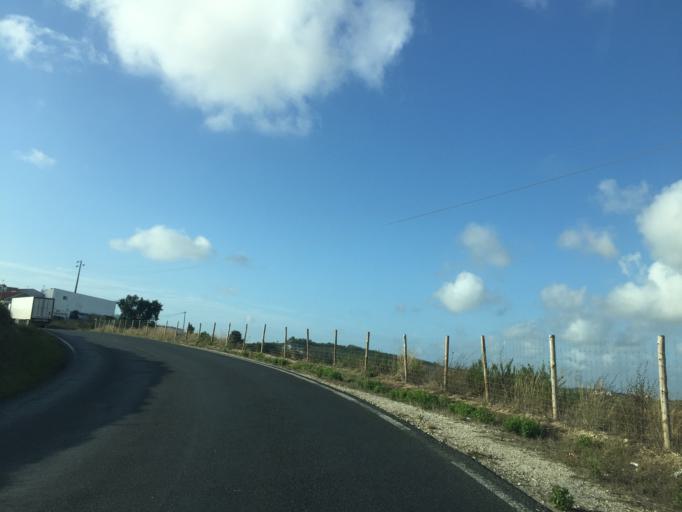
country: PT
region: Lisbon
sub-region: Torres Vedras
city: Torres Vedras
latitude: 39.1150
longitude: -9.2613
